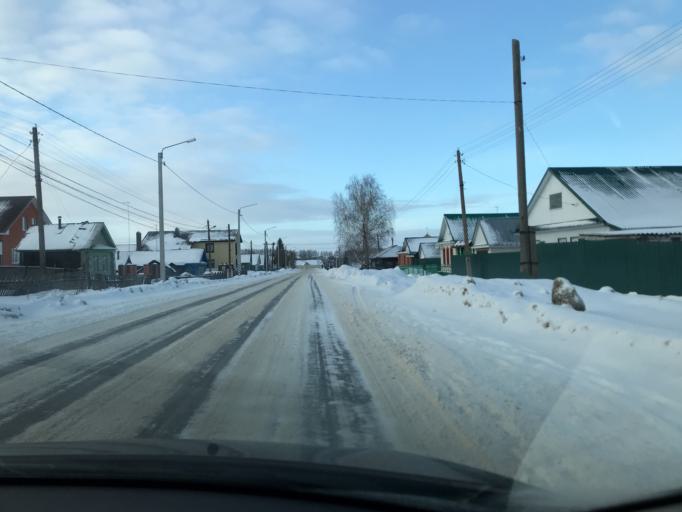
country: RU
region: Ulyanovsk
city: Undory
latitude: 54.6072
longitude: 48.3973
